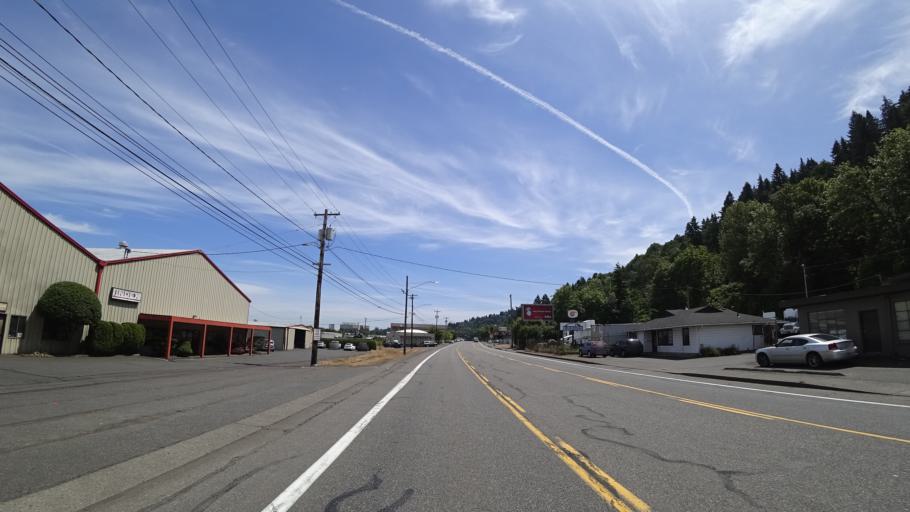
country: US
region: Oregon
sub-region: Multnomah County
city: Portland
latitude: 45.5464
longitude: -122.7240
